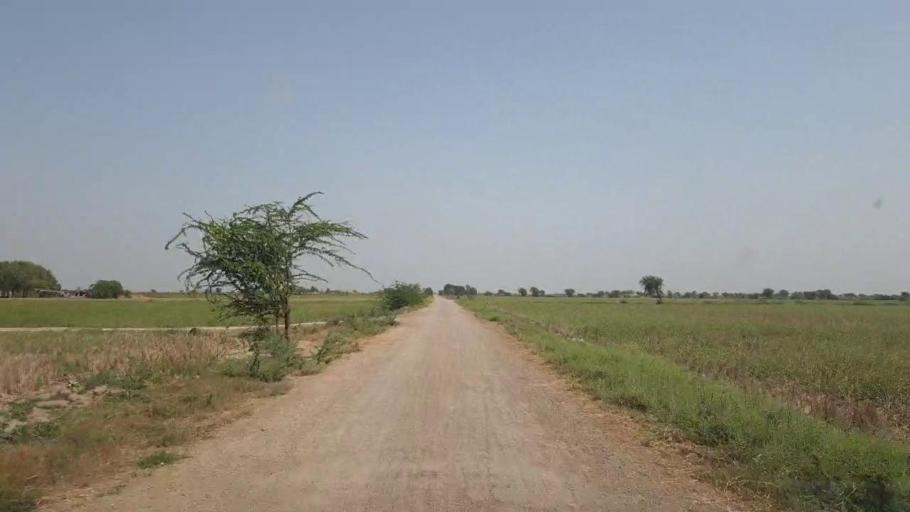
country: PK
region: Sindh
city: Jati
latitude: 24.4775
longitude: 68.5667
